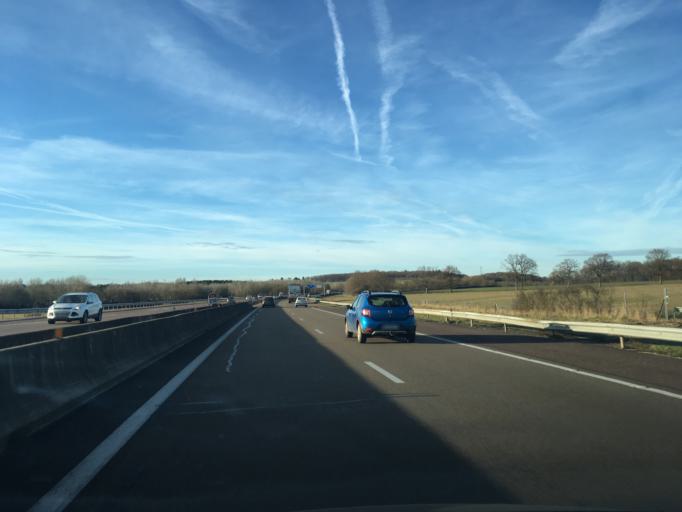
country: FR
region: Bourgogne
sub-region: Departement de l'Yonne
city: Avallon
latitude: 47.5103
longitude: 4.0001
